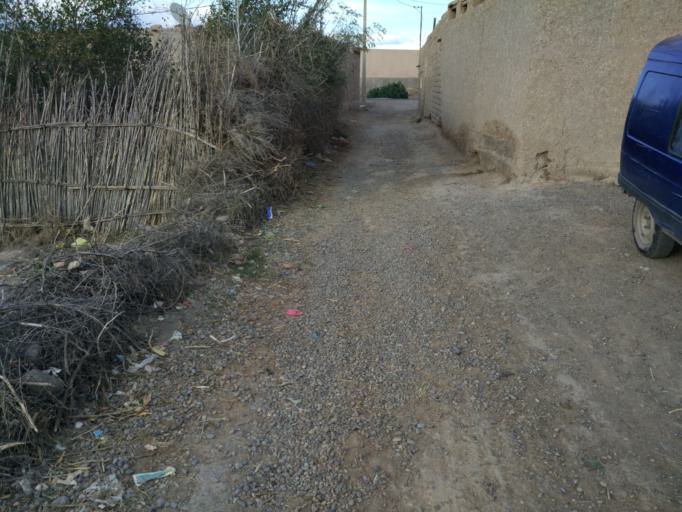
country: MA
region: Marrakech-Tensift-Al Haouz
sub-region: Marrakech
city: Marrakesh
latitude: 31.6418
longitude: -8.2850
